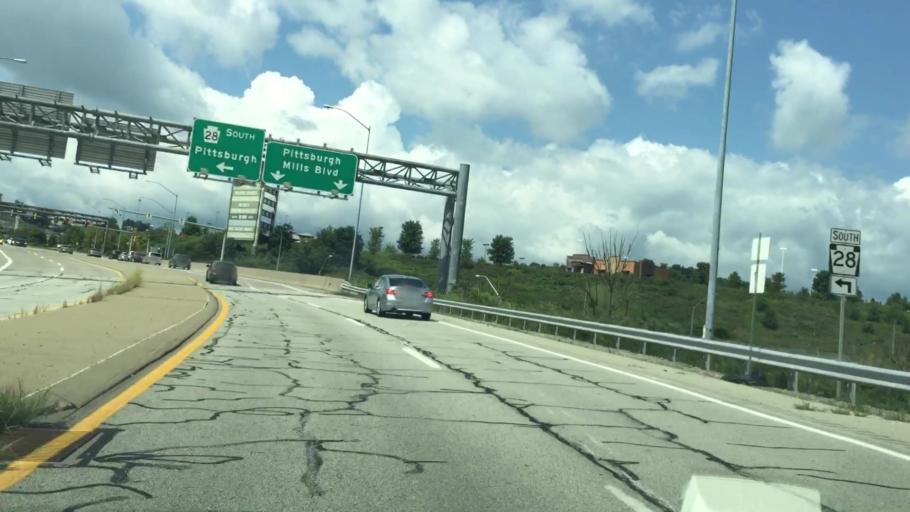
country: US
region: Pennsylvania
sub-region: Allegheny County
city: Cheswick
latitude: 40.5678
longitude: -79.7965
